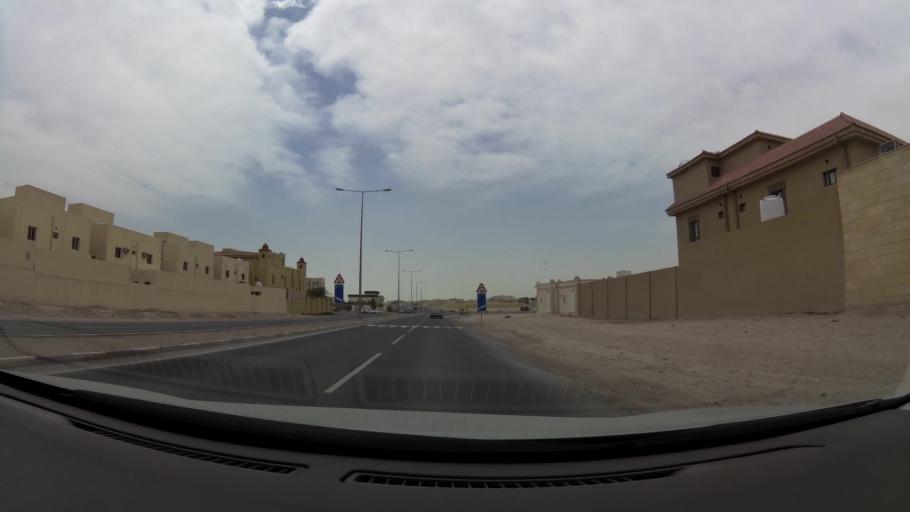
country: QA
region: Baladiyat ad Dawhah
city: Doha
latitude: 25.2228
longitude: 51.4689
